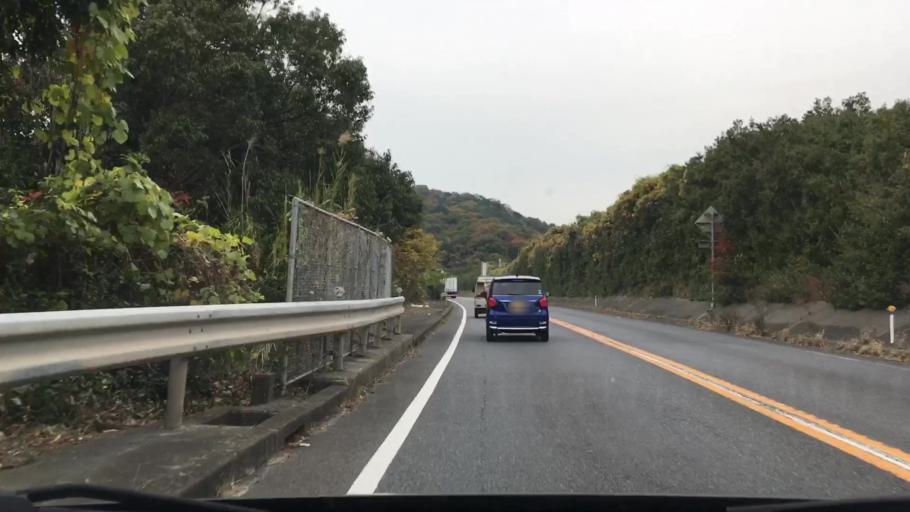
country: JP
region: Yamaguchi
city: Hofu
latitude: 34.0692
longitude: 131.6002
